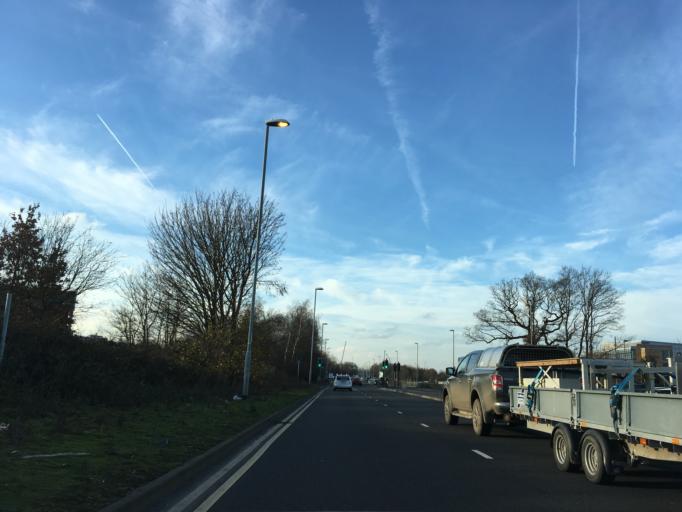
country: GB
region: England
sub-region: Manchester
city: Ringway
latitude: 53.3658
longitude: -2.2620
